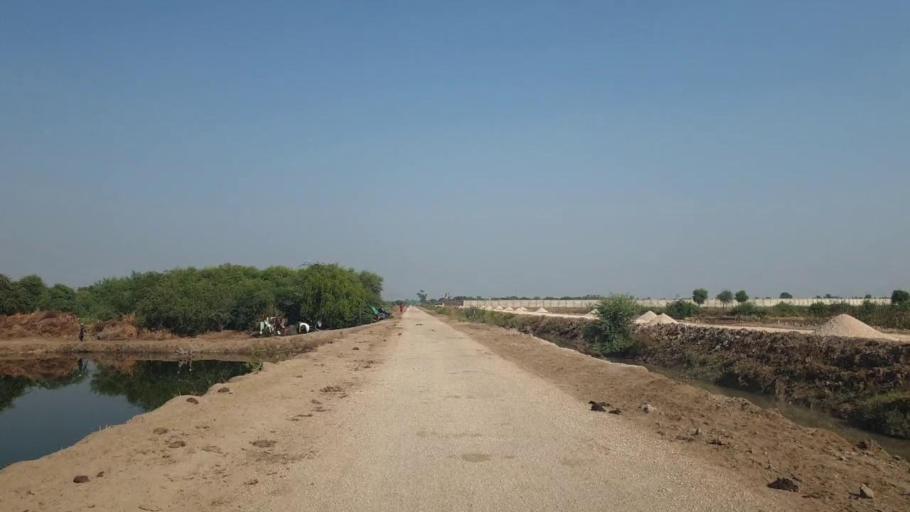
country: PK
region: Sindh
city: Hyderabad
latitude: 25.4722
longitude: 68.3839
